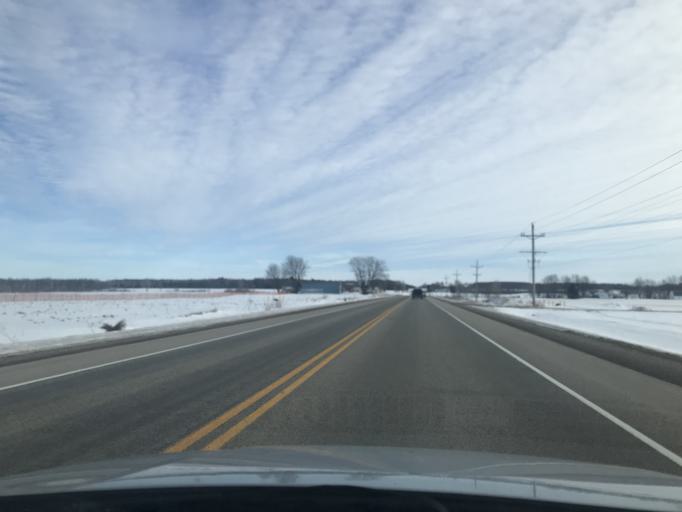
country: US
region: Wisconsin
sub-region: Oconto County
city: Oconto Falls
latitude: 44.8957
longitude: -88.2232
